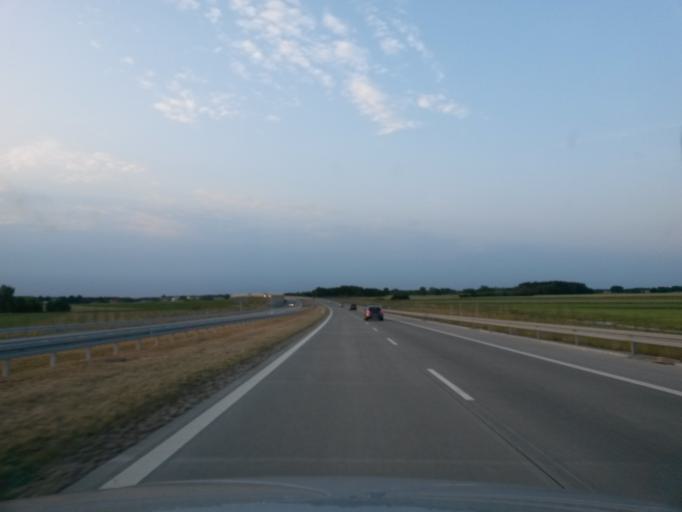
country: PL
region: Lodz Voivodeship
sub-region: Powiat sieradzki
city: Zloczew
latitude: 51.4100
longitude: 18.6364
